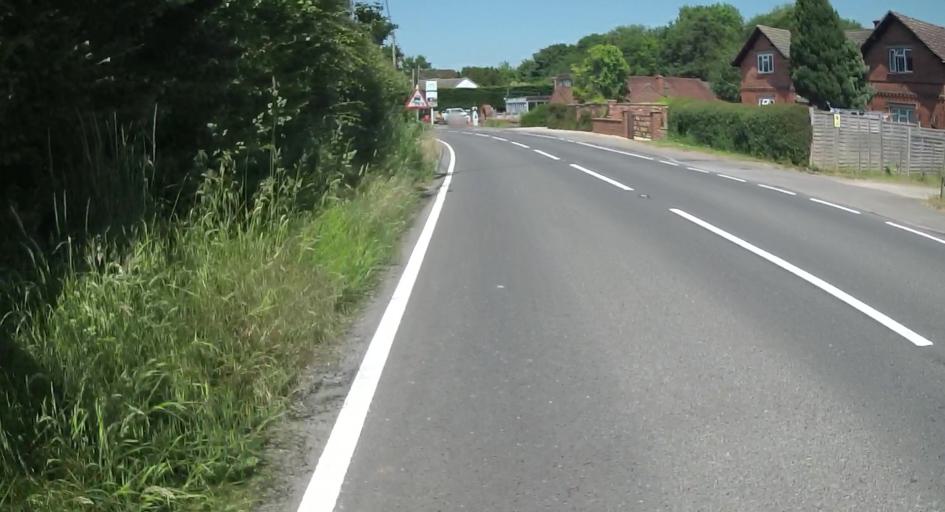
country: GB
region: England
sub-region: Hampshire
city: Kingsclere
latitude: 51.3525
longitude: -1.2042
